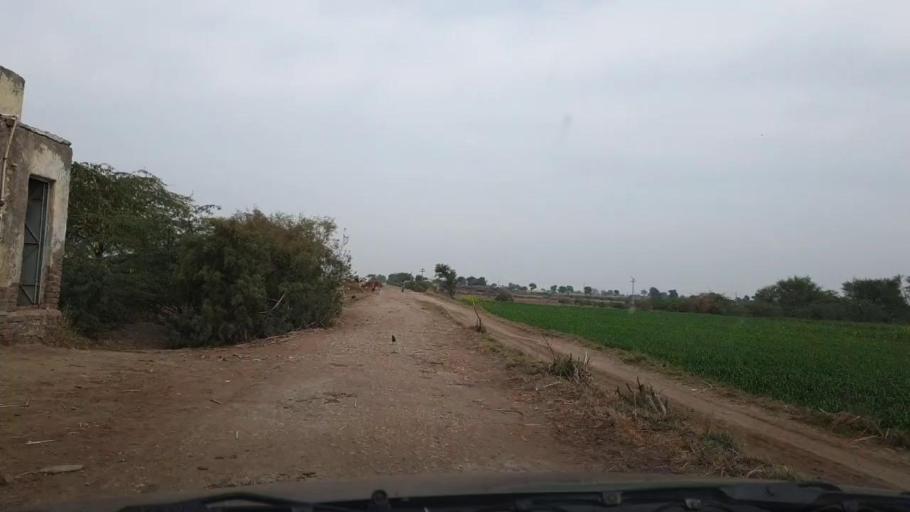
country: PK
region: Sindh
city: Sanghar
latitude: 26.1071
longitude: 68.8963
